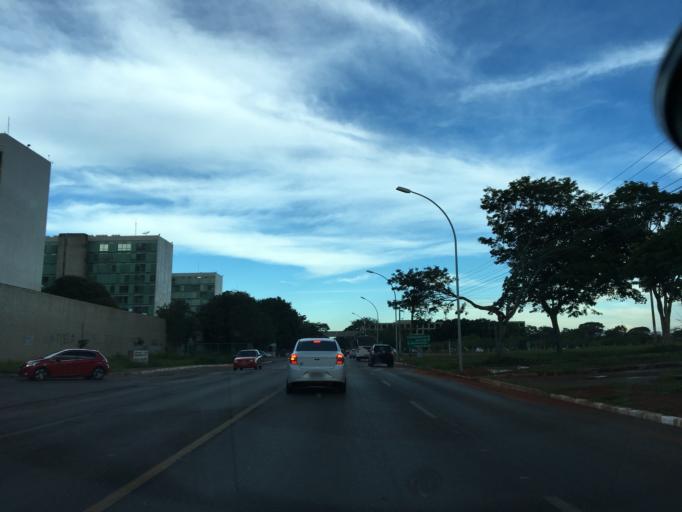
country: BR
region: Federal District
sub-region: Brasilia
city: Brasilia
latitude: -15.7994
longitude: -47.8747
